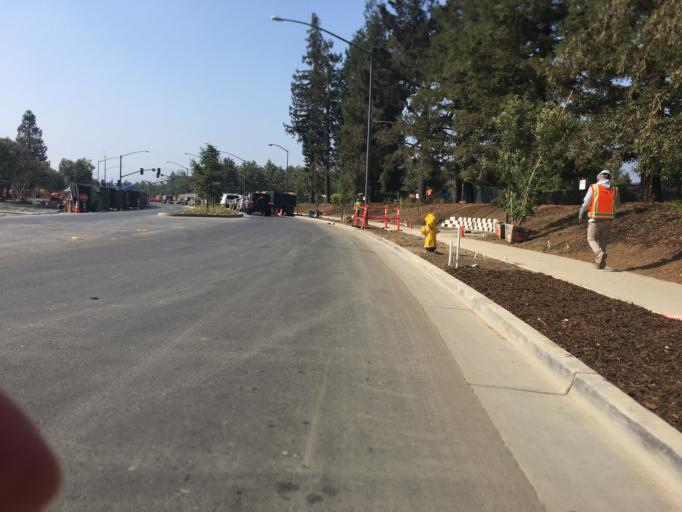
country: US
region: California
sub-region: Santa Clara County
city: Cupertino
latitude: 37.3336
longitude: -122.0057
